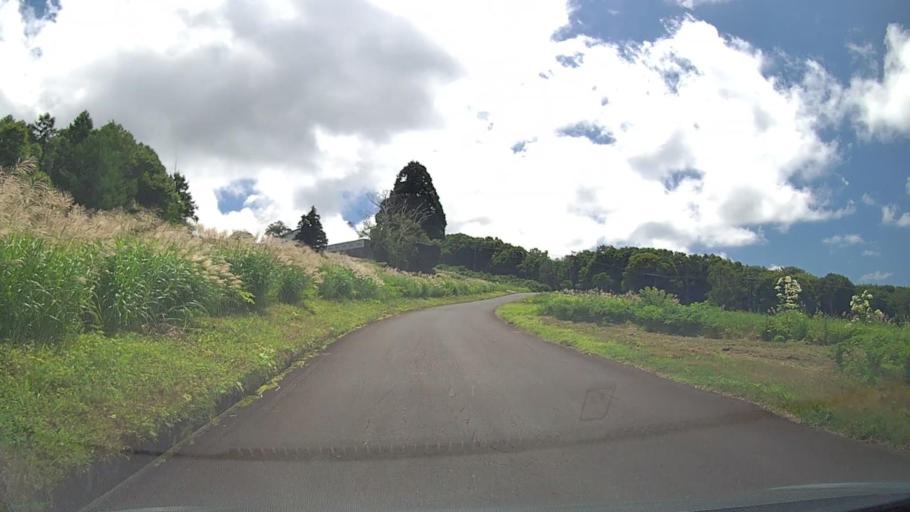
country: JP
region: Nagano
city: Iiyama
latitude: 36.9242
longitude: 138.4748
